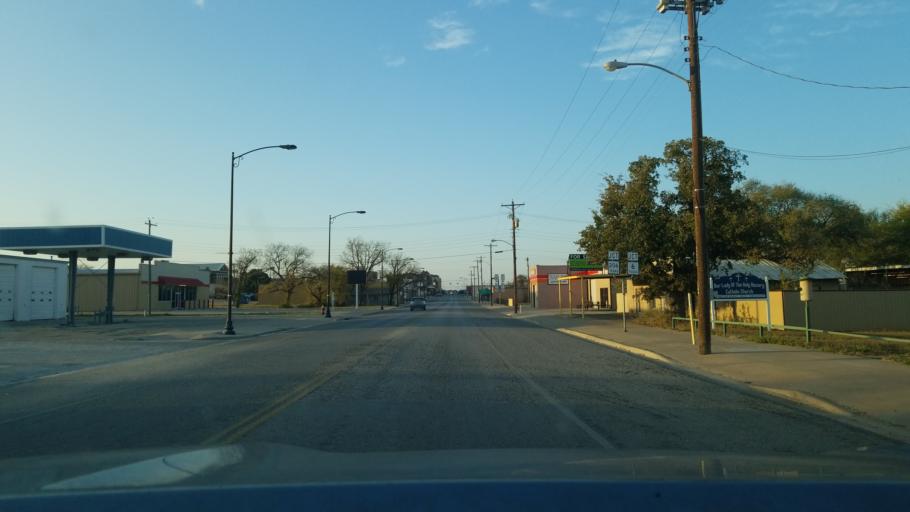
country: US
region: Texas
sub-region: Eastland County
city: Cisco
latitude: 32.3847
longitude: -98.9771
